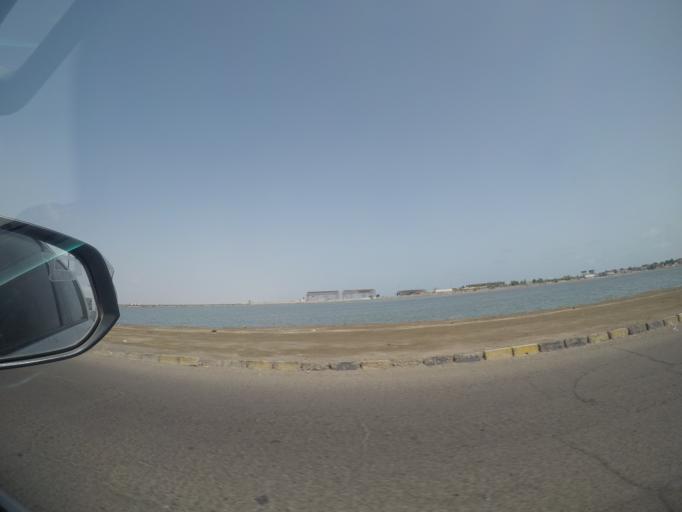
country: YE
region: Aden
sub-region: Khur Maksar
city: Khawr Maksar
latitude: 12.8212
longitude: 45.0363
